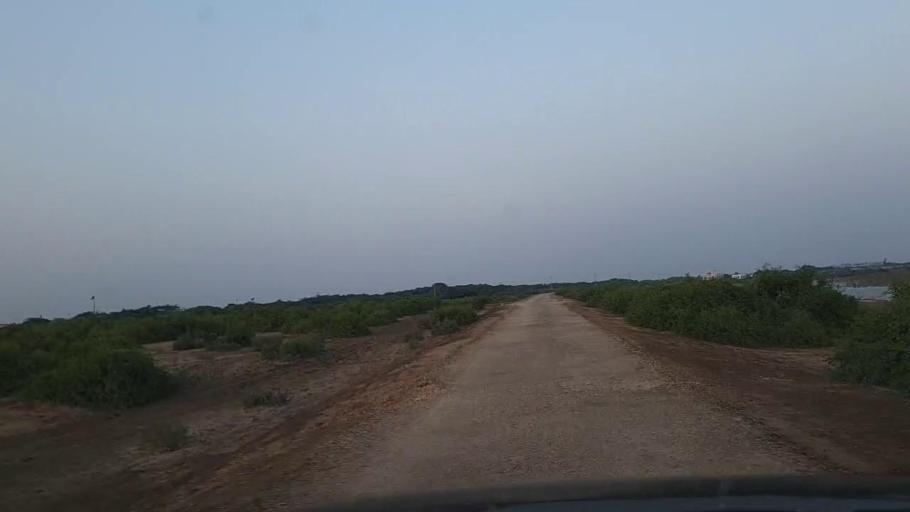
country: PK
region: Sindh
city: Mirpur Sakro
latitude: 24.6366
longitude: 67.6610
